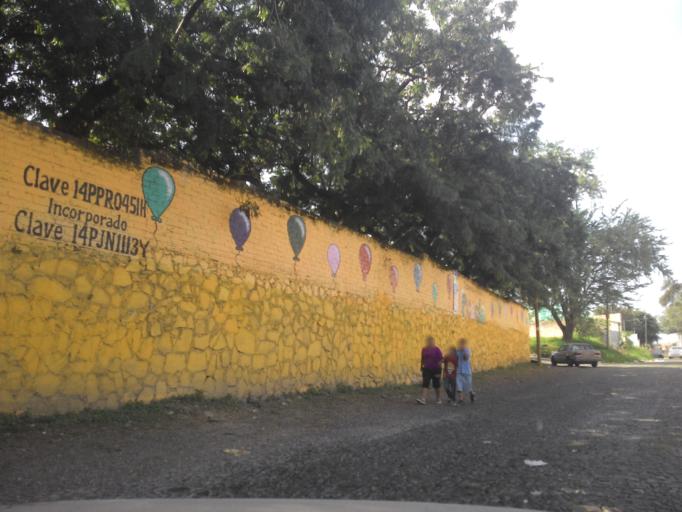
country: MX
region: Jalisco
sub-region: Tlajomulco de Zuniga
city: Altus Bosques
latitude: 20.5870
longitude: -103.3848
